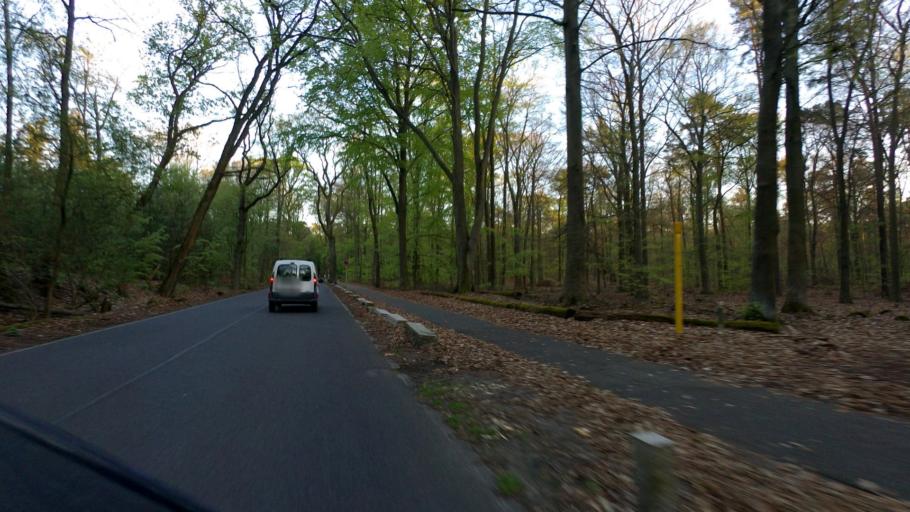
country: DE
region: Berlin
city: Nikolassee
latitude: 52.4502
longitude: 13.1942
